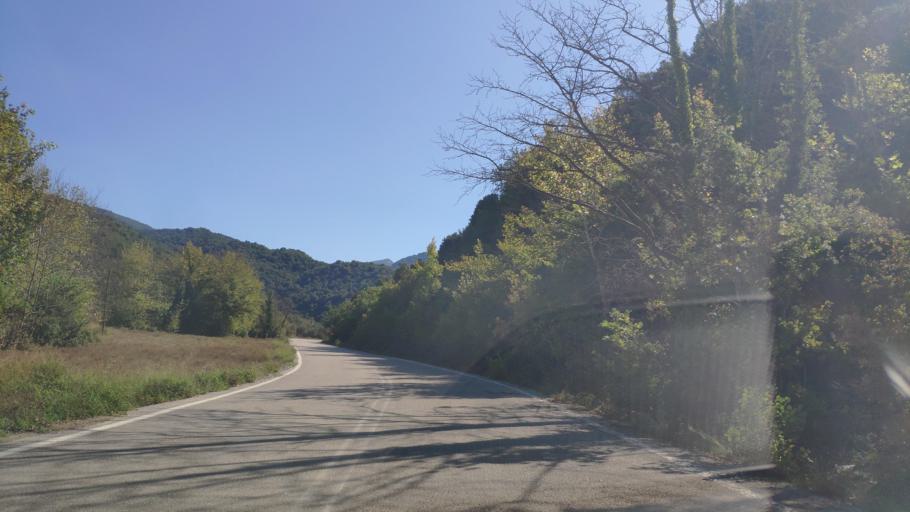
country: GR
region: West Greece
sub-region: Nomos Aitolias kai Akarnanias
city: Sardinia
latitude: 38.9235
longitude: 21.3704
